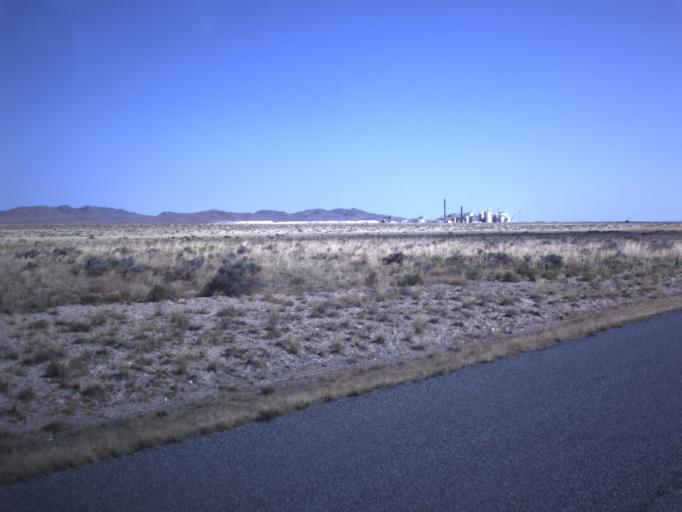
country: US
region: Utah
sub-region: Millard County
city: Fillmore
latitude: 38.9179
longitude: -112.8128
